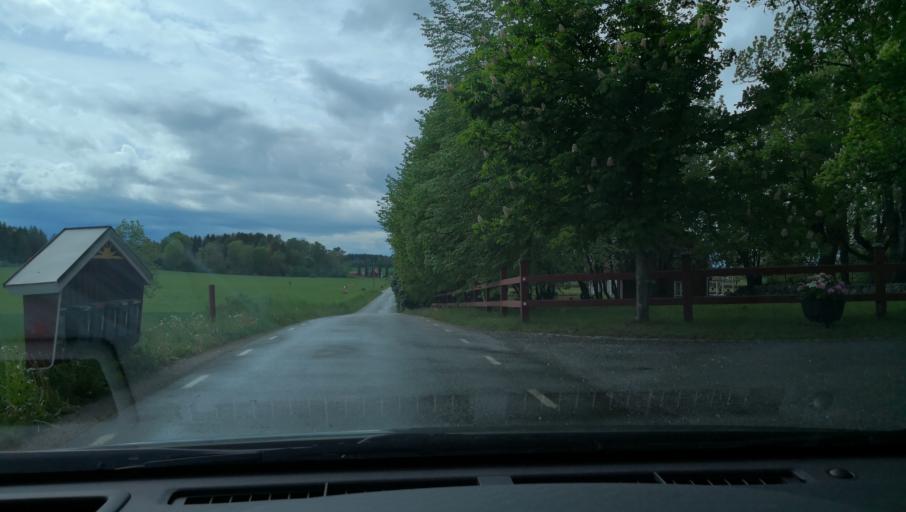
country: SE
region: Uppsala
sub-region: Enkopings Kommun
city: Orsundsbro
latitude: 59.7246
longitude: 17.4152
